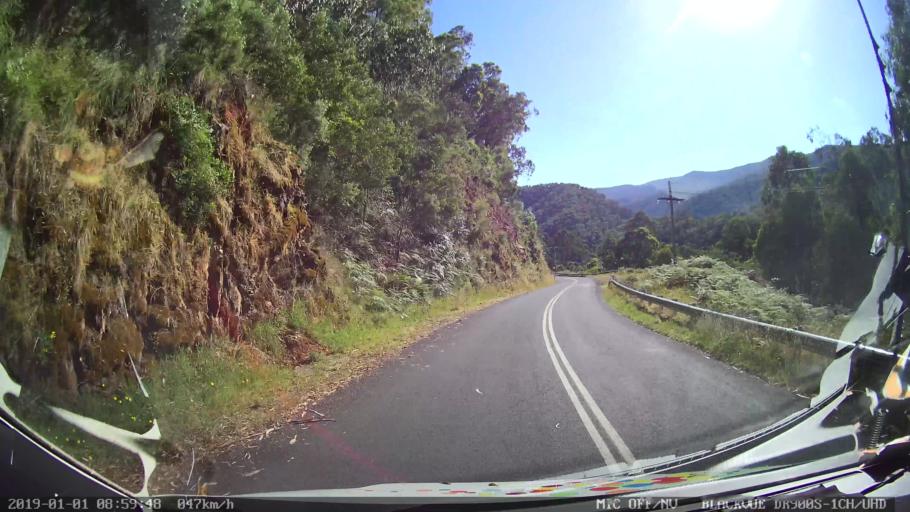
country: AU
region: New South Wales
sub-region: Snowy River
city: Jindabyne
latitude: -36.2388
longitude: 148.1792
